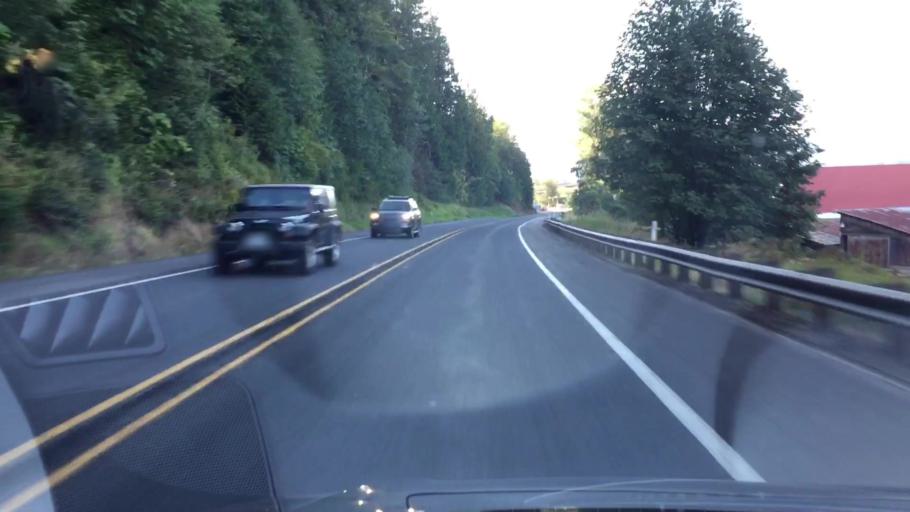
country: US
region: Washington
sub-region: Lewis County
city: Morton
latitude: 46.5281
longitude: -122.2367
